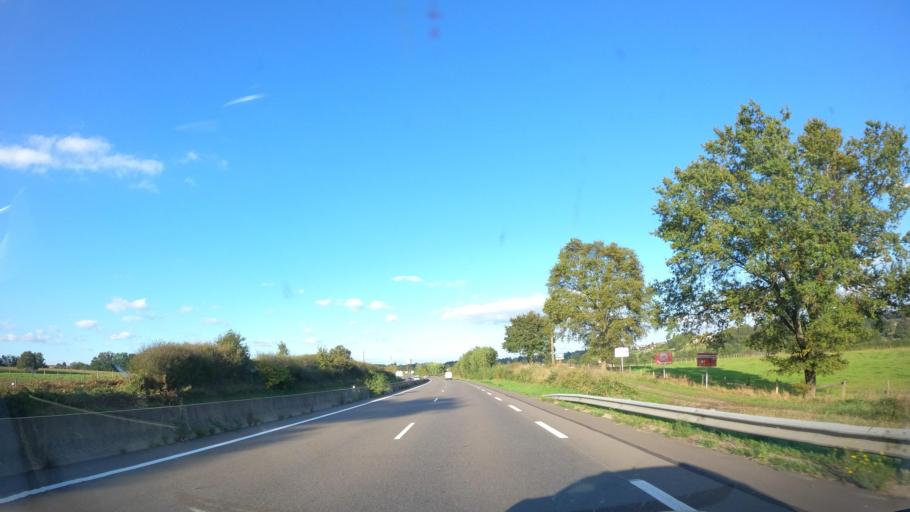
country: FR
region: Bourgogne
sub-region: Departement de Saone-et-Loire
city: Ciry-le-Noble
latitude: 46.6367
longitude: 4.3255
